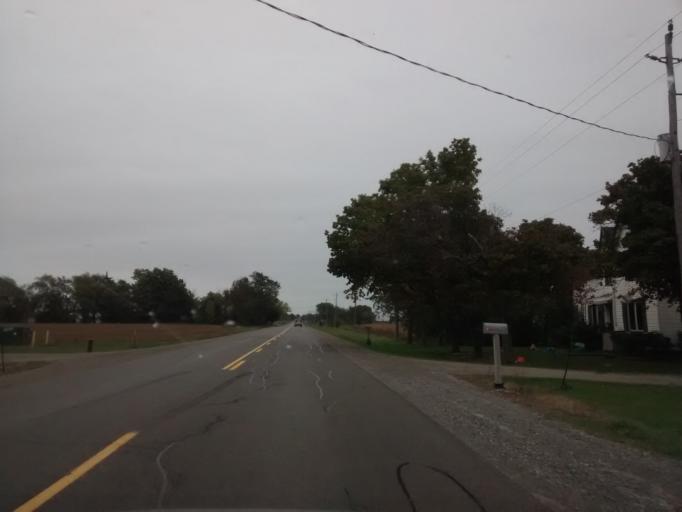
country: CA
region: Ontario
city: Ancaster
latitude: 42.8497
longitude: -79.8369
